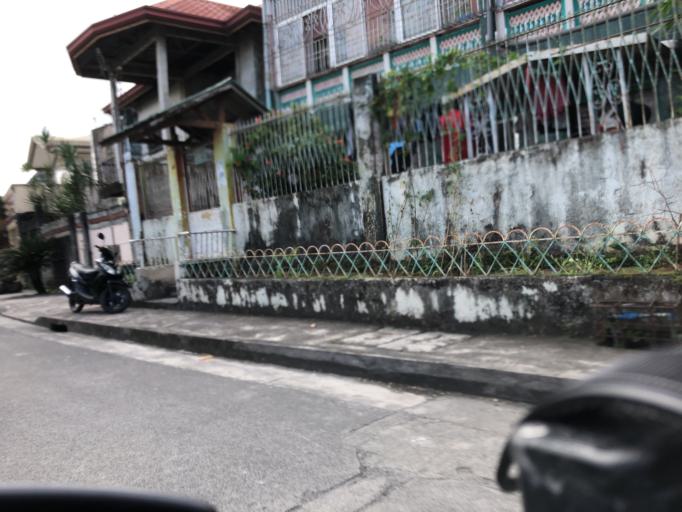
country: PH
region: Central Luzon
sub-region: Province of Bulacan
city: San Jose del Monte
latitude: 14.7617
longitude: 121.0512
